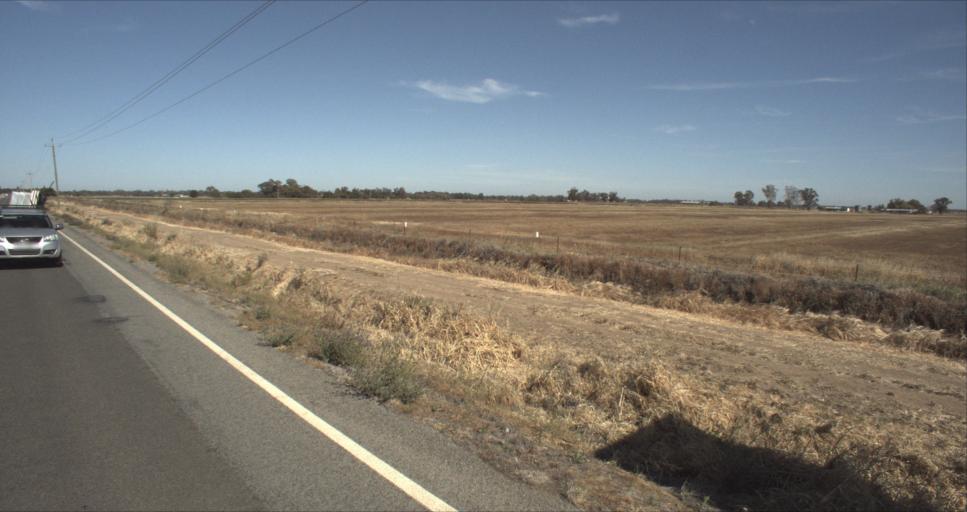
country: AU
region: New South Wales
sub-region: Leeton
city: Leeton
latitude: -34.5573
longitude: 146.4468
